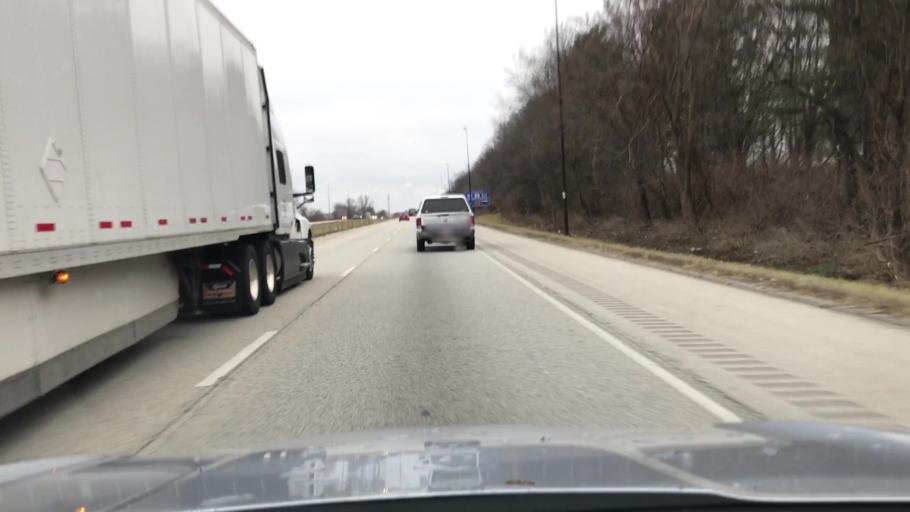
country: US
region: Illinois
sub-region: Sangamon County
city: Grandview
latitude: 39.8180
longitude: -89.5930
